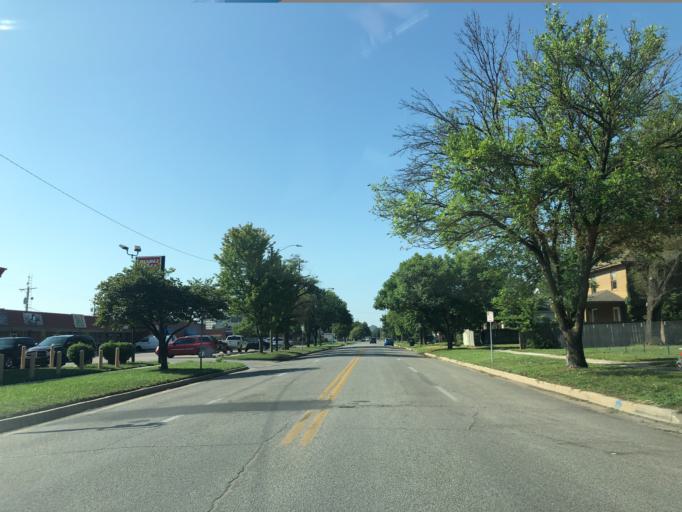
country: US
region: Kansas
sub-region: Sedgwick County
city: Wichita
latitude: 37.7028
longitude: -97.3420
